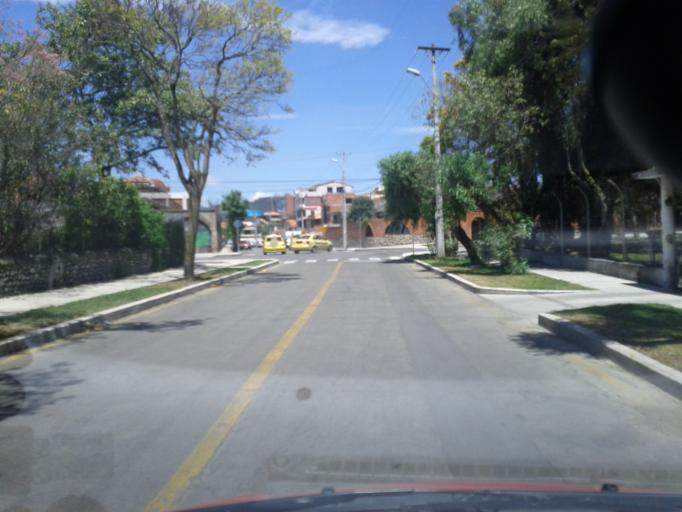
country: EC
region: Azuay
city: Cuenca
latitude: -2.9035
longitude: -79.0089
